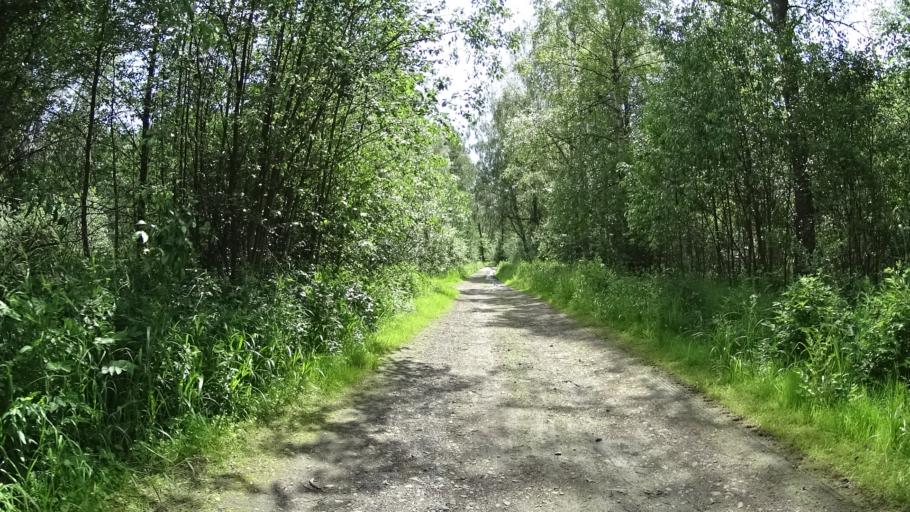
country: FI
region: Uusimaa
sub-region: Raaseporin
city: Pohja
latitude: 60.1059
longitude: 23.5481
